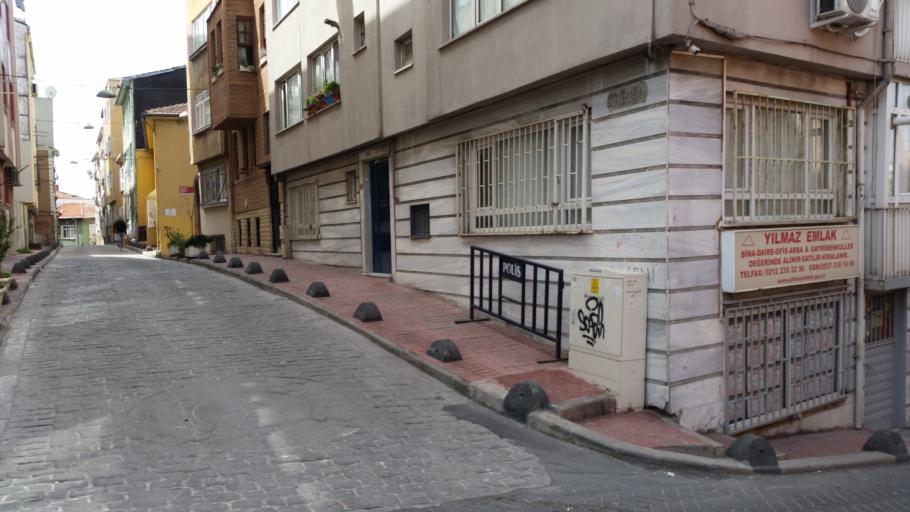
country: TR
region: Istanbul
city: Eminoenue
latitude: 41.0322
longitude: 28.9711
